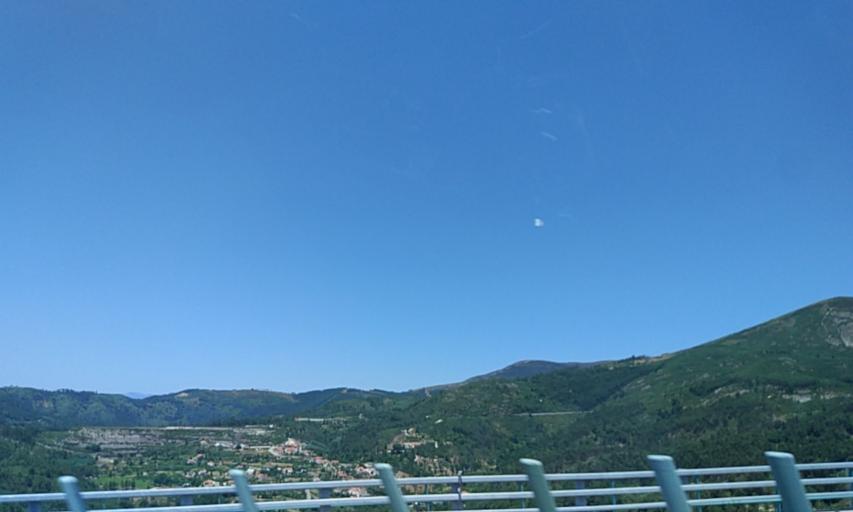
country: PT
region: Porto
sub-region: Amarante
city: Amarante
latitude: 41.2531
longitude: -7.9907
